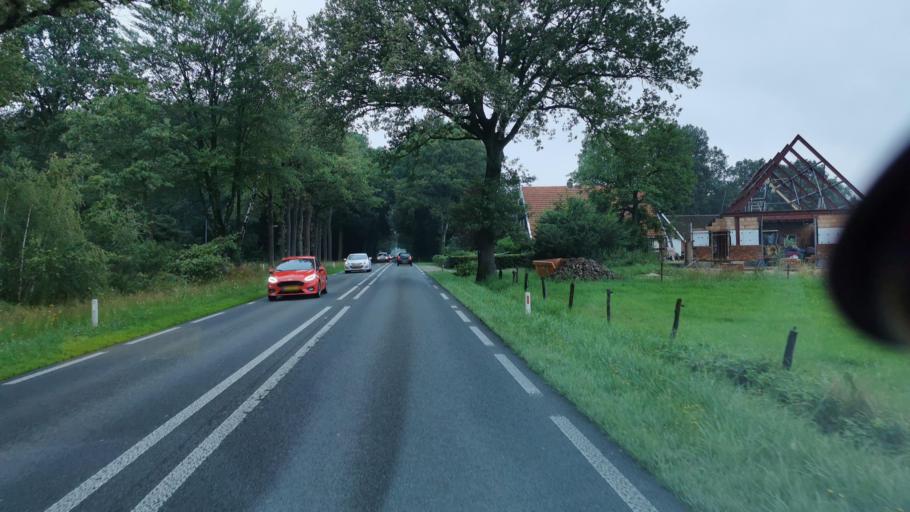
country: NL
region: Overijssel
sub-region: Gemeente Losser
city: Losser
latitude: 52.2759
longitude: 6.9770
